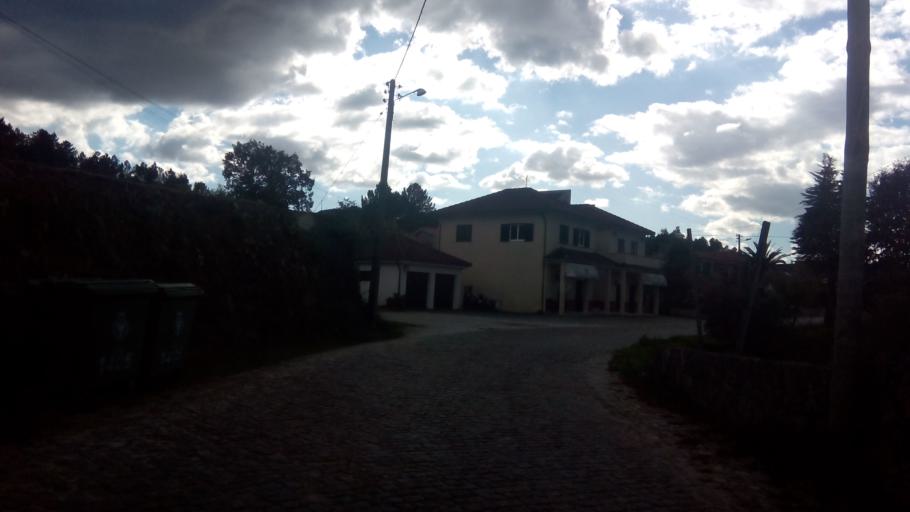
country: PT
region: Porto
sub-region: Amarante
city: Amarante
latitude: 41.2700
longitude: -8.0020
